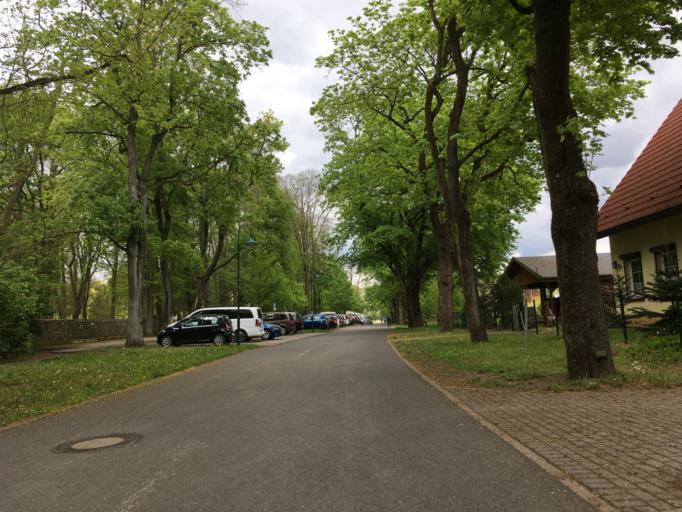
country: DE
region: Brandenburg
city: Bernau bei Berlin
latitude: 52.6816
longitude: 13.5323
